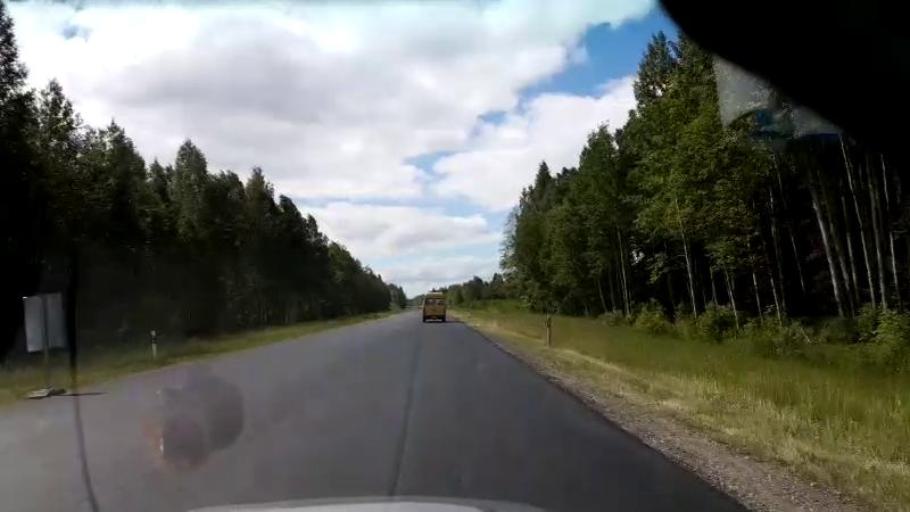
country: LV
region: Salacgrivas
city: Ainazi
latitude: 57.9805
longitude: 24.4589
